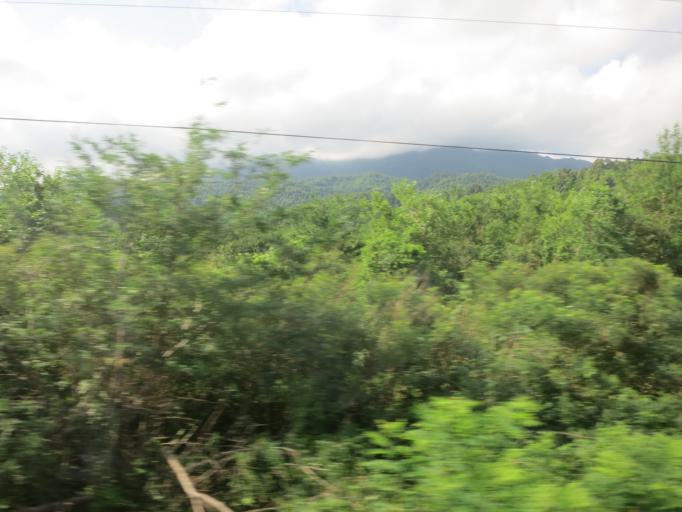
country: GE
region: Samegrelo and Zemo Svaneti
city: Abasha
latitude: 42.0951
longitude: 42.2250
